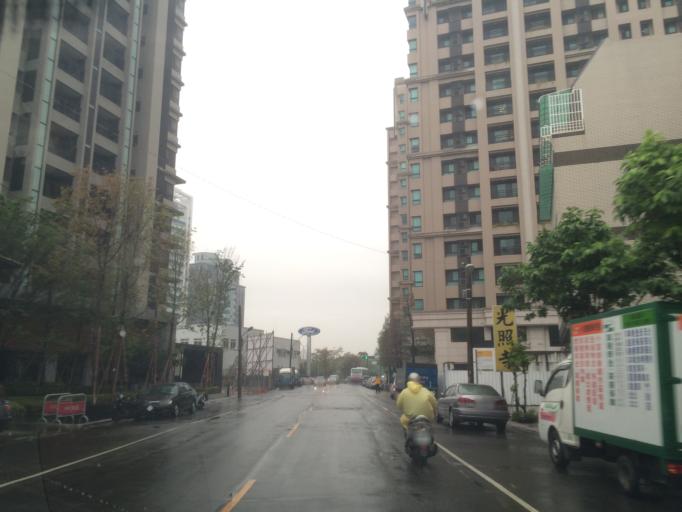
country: TW
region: Taiwan
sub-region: Taichung City
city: Taichung
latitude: 24.1842
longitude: 120.6875
